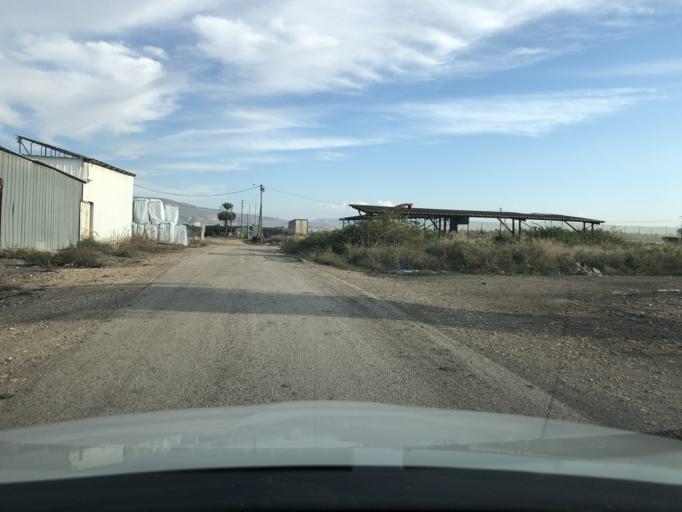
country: IL
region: Northern District
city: Yavne'el
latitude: 32.6561
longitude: 35.5815
